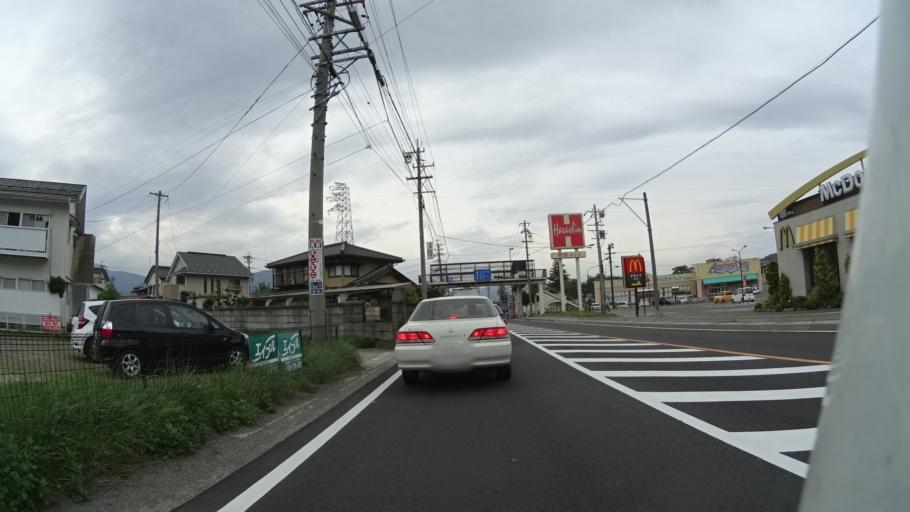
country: JP
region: Nagano
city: Nagano-shi
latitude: 36.5199
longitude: 138.1289
